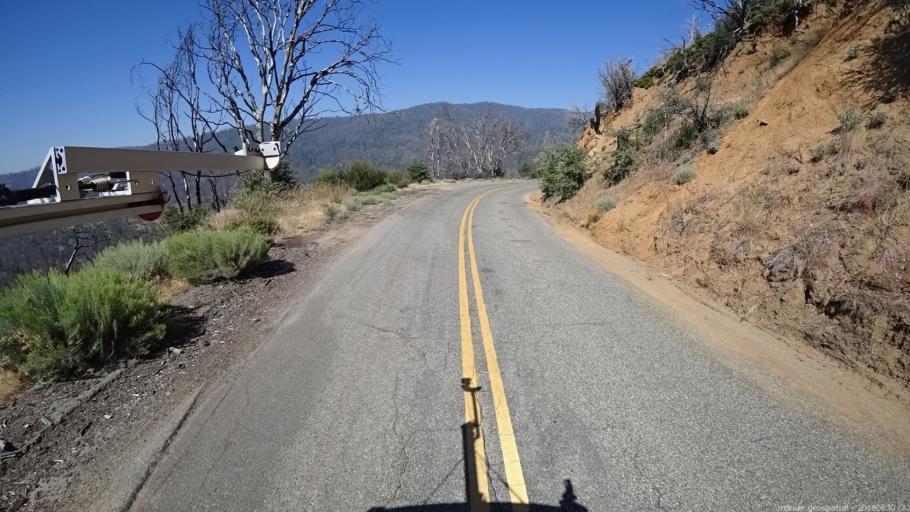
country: US
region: California
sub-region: Fresno County
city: Auberry
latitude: 37.2961
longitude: -119.3508
